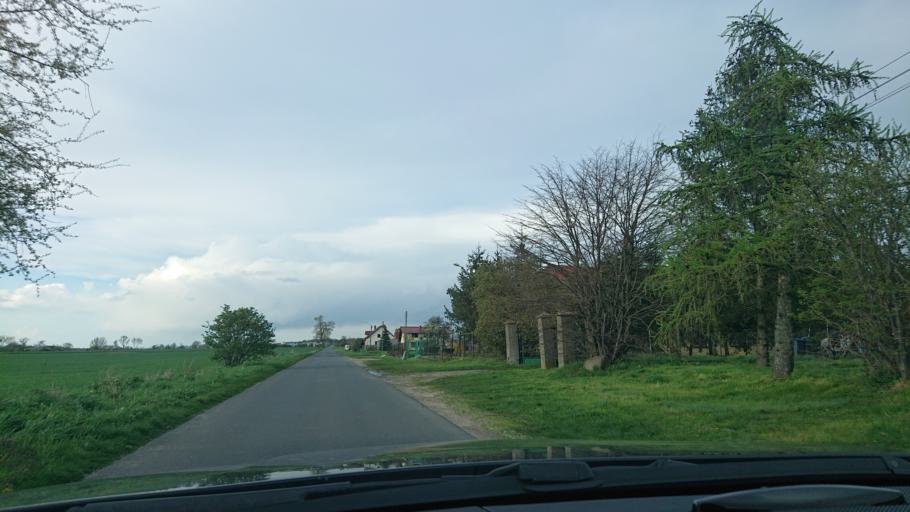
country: PL
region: Greater Poland Voivodeship
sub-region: Powiat gnieznienski
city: Klecko
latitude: 52.5810
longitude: 17.4814
